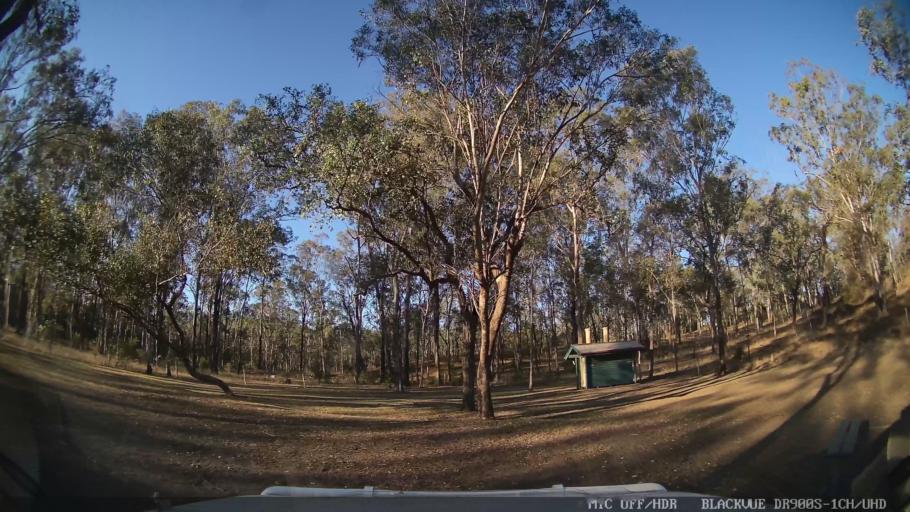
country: AU
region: Queensland
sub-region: Gladstone
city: Toolooa
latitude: -24.6717
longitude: 151.3282
